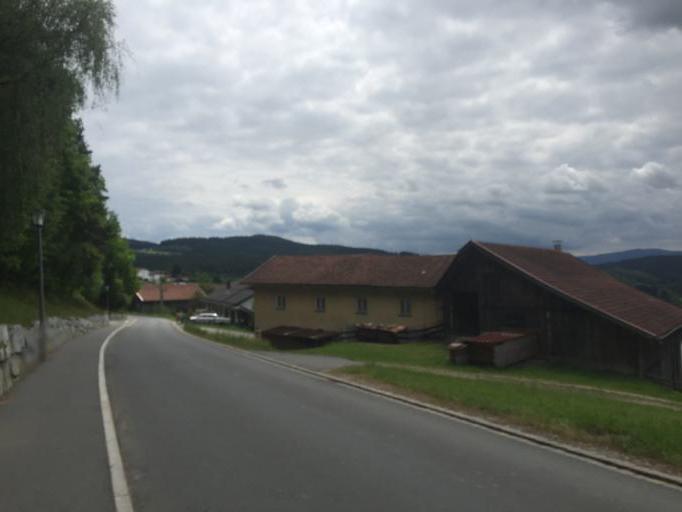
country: DE
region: Bavaria
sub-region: Lower Bavaria
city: Patersdorf
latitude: 49.0179
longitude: 13.0246
